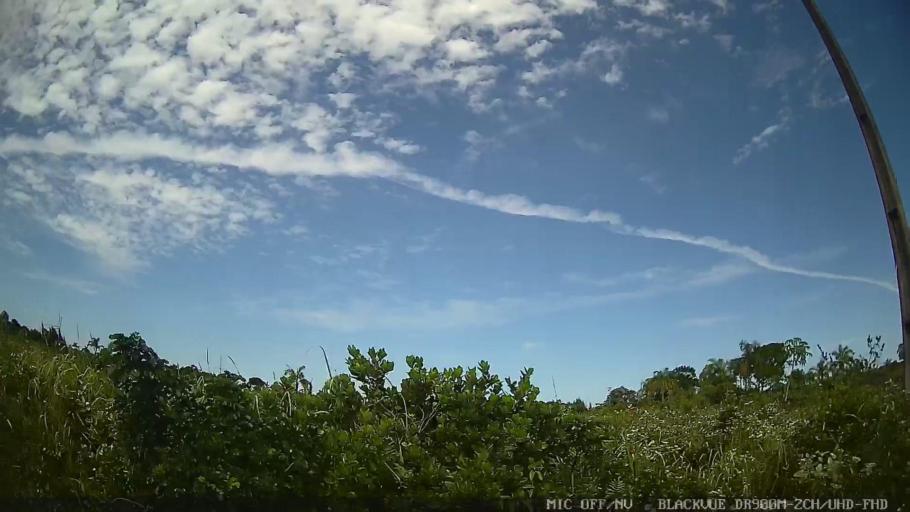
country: BR
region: Sao Paulo
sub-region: Iguape
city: Iguape
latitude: -24.7141
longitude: -47.5112
